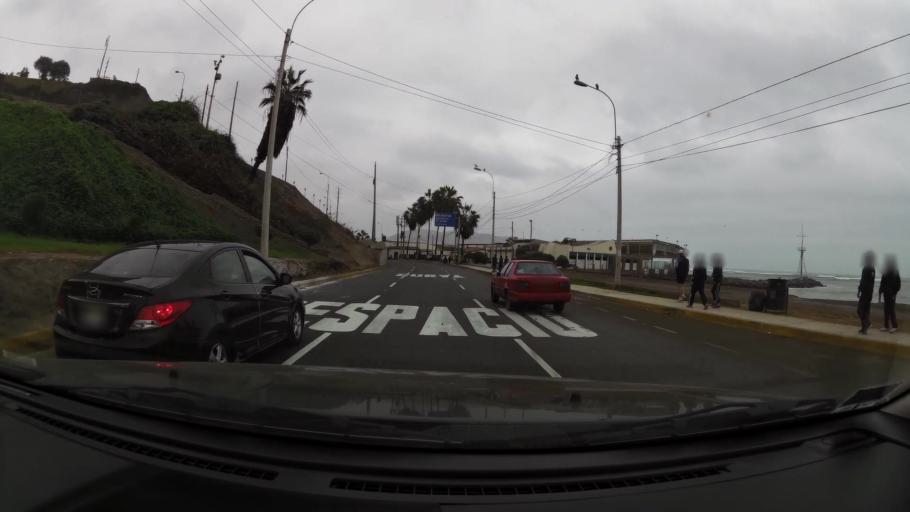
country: PE
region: Lima
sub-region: Lima
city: Surco
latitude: -12.1391
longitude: -77.0282
